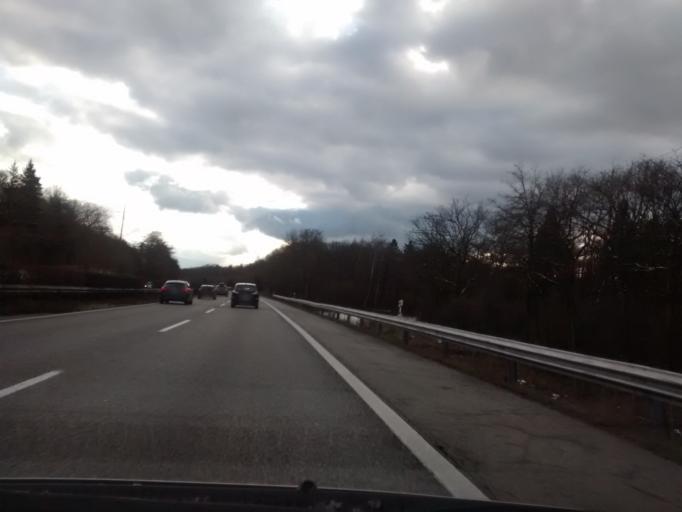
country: FR
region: Rhone-Alpes
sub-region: Departement de l'Ain
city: Sauverny
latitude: 46.3123
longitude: 6.1439
